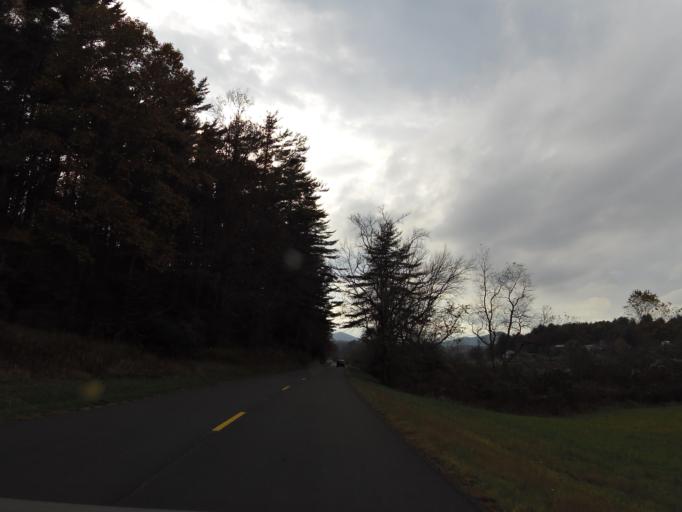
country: US
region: North Carolina
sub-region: Alleghany County
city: Sparta
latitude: 36.3951
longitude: -81.2280
